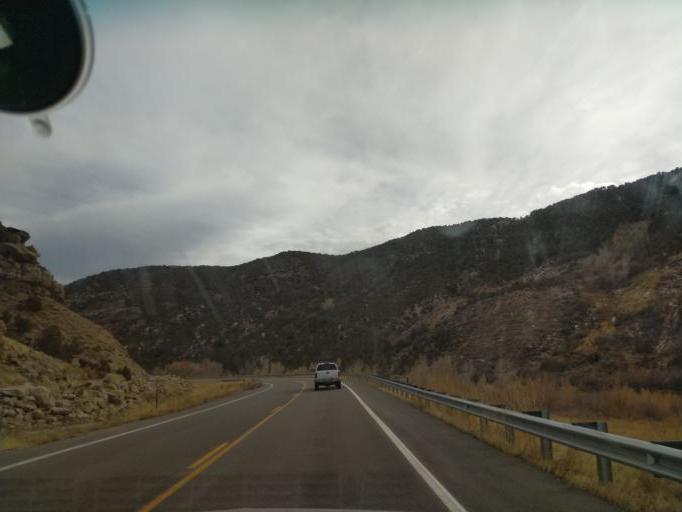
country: US
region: Colorado
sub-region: Mesa County
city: Palisade
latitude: 39.1975
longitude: -108.1881
